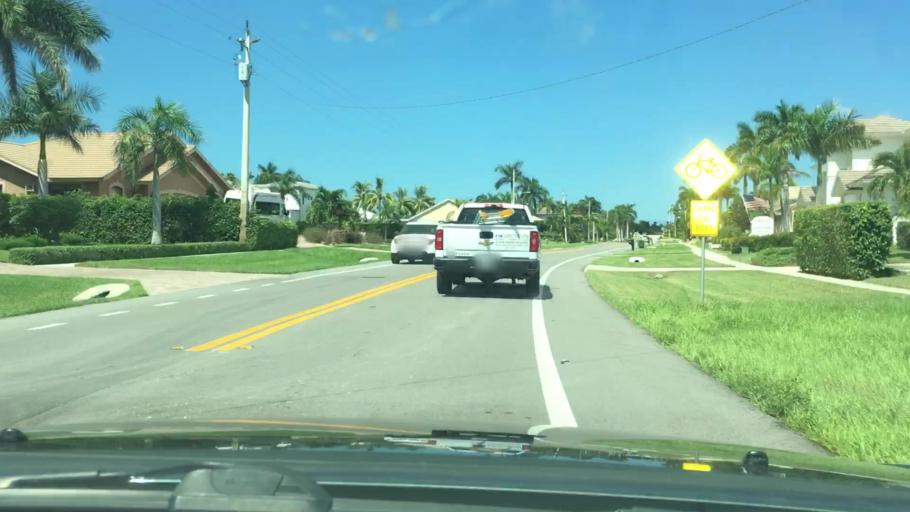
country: US
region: Florida
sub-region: Collier County
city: Marco
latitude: 25.9482
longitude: -81.7348
